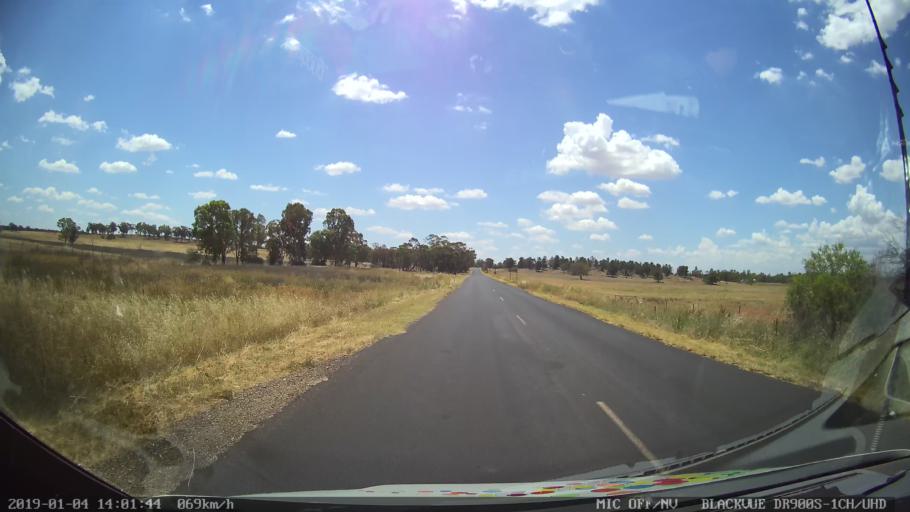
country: AU
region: New South Wales
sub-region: Dubbo Municipality
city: Dubbo
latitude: -32.2937
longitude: 148.5988
